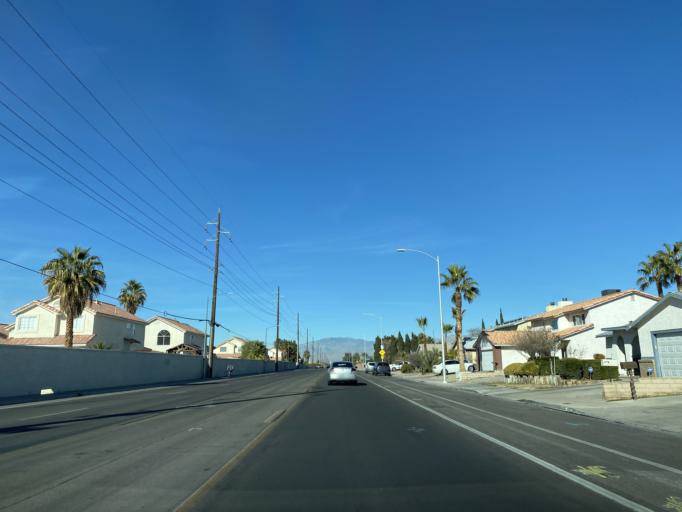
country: US
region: Nevada
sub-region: Clark County
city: Spring Valley
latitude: 36.1839
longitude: -115.2510
